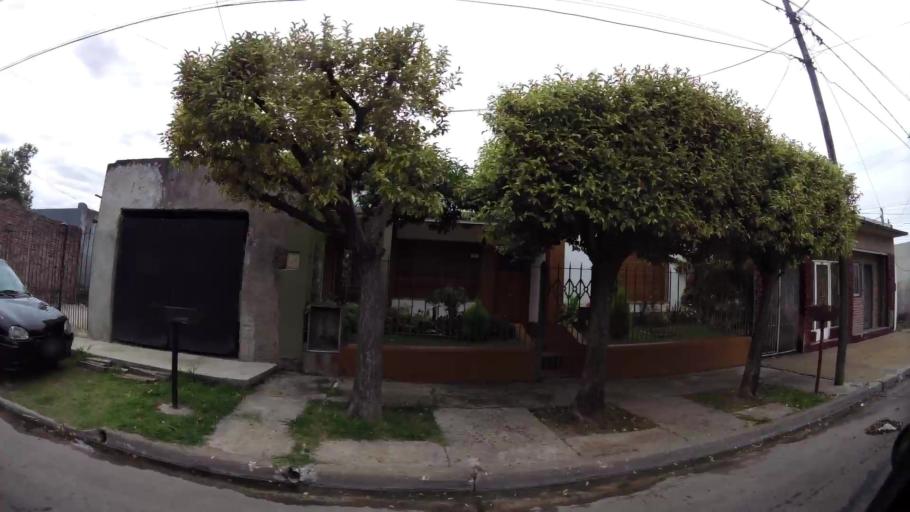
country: AR
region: Buenos Aires
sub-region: Partido de Quilmes
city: Quilmes
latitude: -34.7567
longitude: -58.2229
